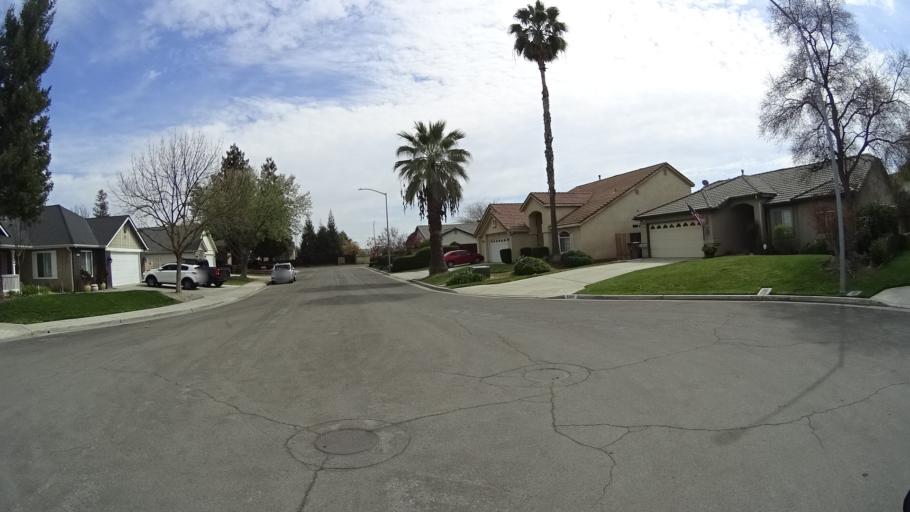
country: US
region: California
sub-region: Fresno County
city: West Park
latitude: 36.8190
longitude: -119.8816
